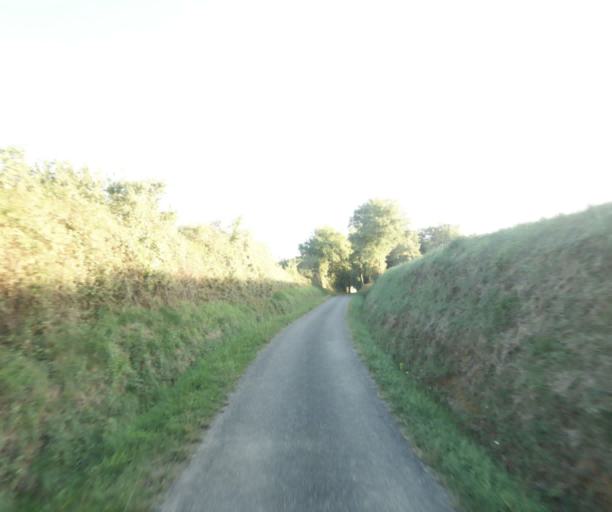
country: FR
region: Midi-Pyrenees
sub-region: Departement du Gers
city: Le Houga
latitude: 43.8319
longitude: -0.1097
